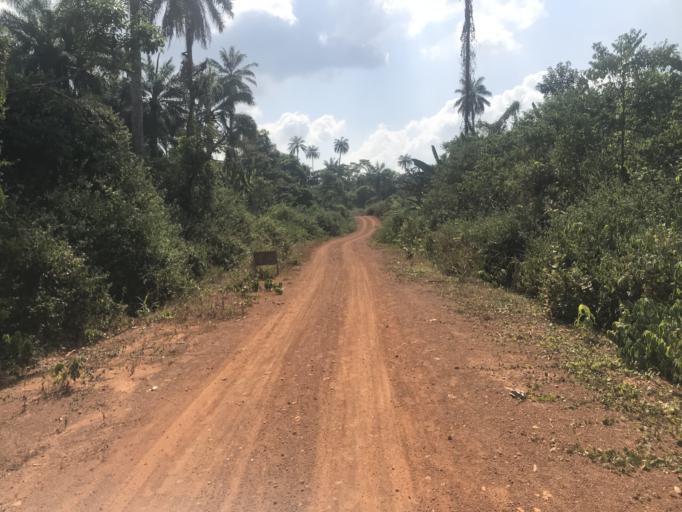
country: NG
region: Osun
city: Ibokun
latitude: 7.8164
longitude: 4.6974
